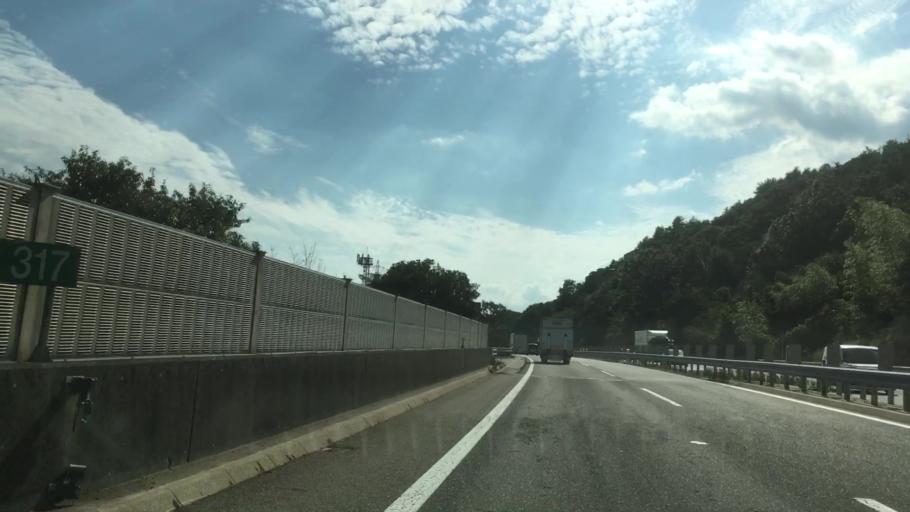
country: JP
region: Hiroshima
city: Ono-hara
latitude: 34.2844
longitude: 132.2616
